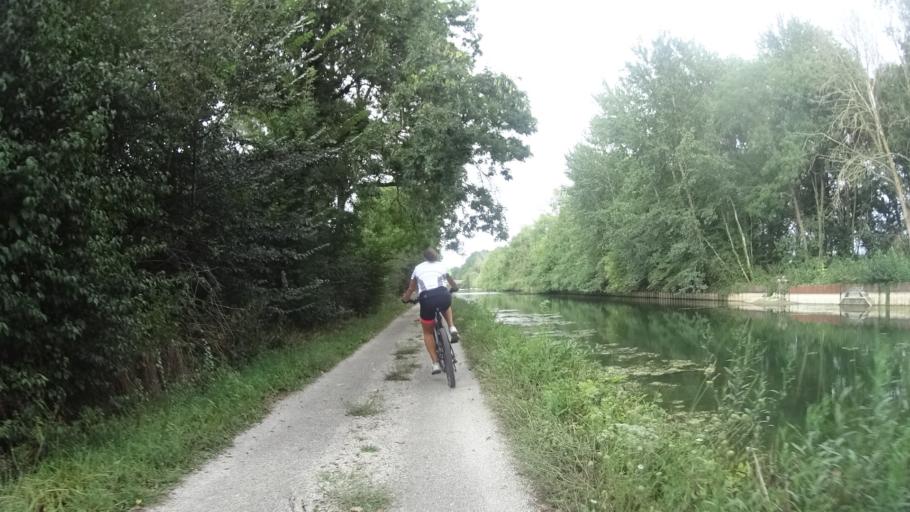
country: FR
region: Picardie
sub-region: Departement de l'Aisne
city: Itancourt
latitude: 49.7591
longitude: 3.3818
